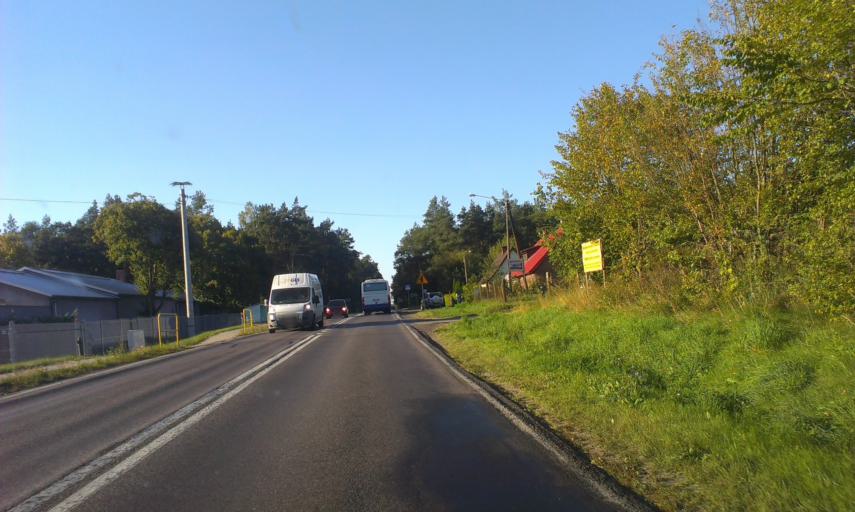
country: PL
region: Kujawsko-Pomorskie
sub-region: Powiat tucholski
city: Cekcyn
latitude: 53.5187
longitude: 17.9526
